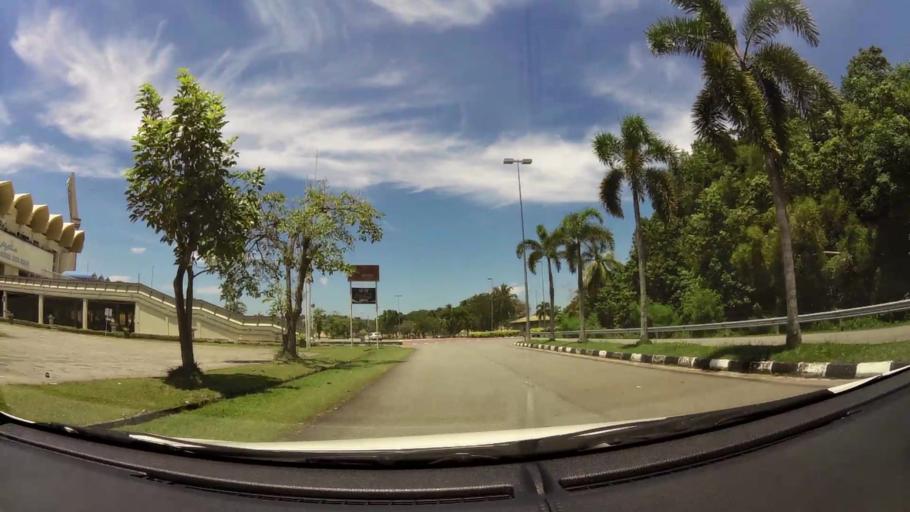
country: BN
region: Brunei and Muara
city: Bandar Seri Begawan
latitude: 4.9297
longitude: 114.9438
